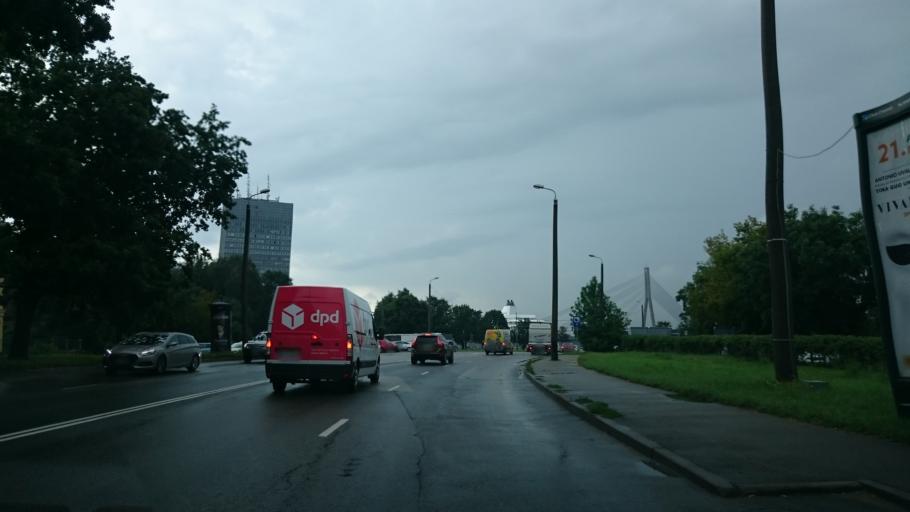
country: LV
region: Riga
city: Riga
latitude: 56.9582
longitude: 24.0980
